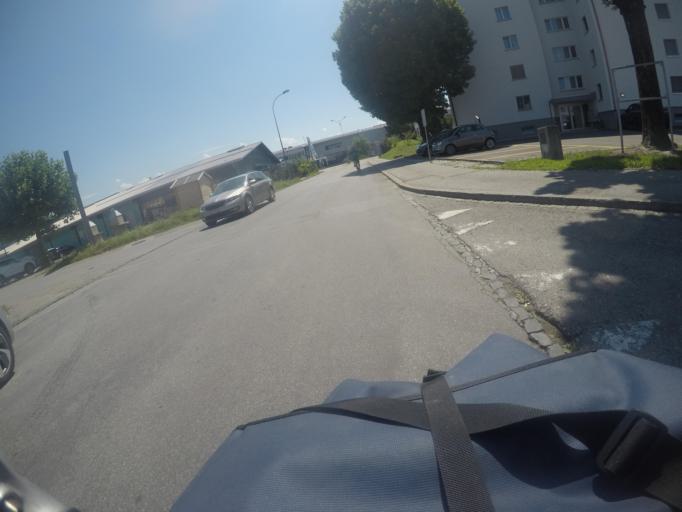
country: CH
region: Saint Gallen
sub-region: Wahlkreis Rheintal
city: Sankt Margrethen
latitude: 47.4474
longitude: 9.6490
